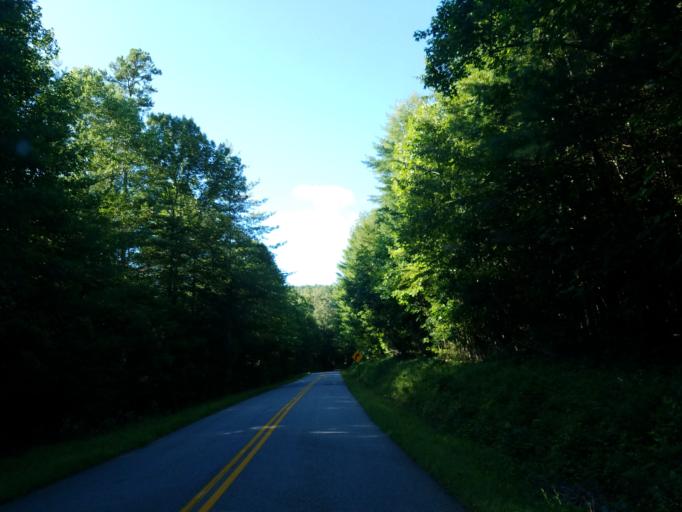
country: US
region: Georgia
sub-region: Union County
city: Blairsville
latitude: 34.7603
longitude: -84.1141
